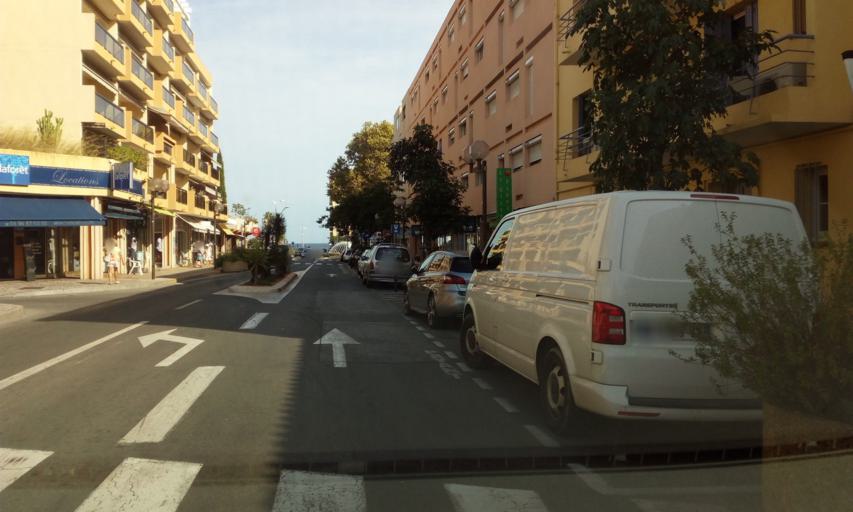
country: FR
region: Provence-Alpes-Cote d'Azur
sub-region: Departement du Var
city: Le Lavandou
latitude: 43.1370
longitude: 6.3648
